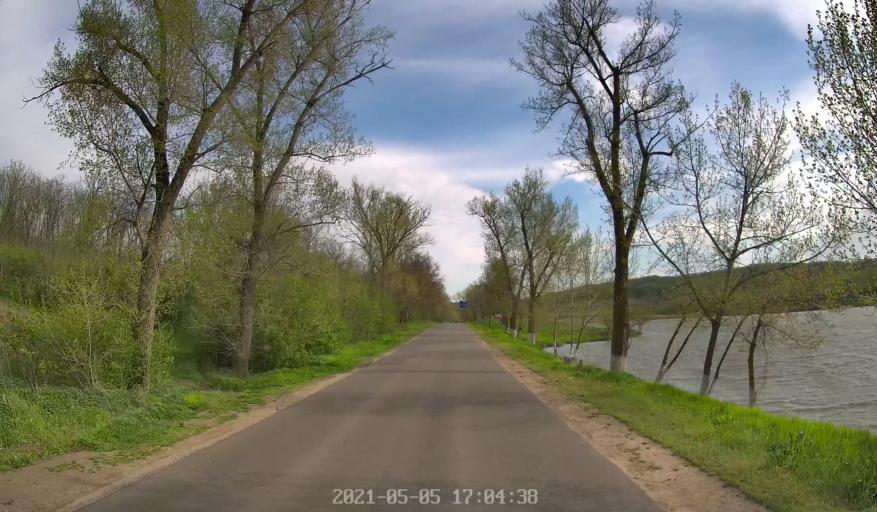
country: MD
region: Chisinau
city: Vadul lui Voda
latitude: 47.0387
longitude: 29.1362
